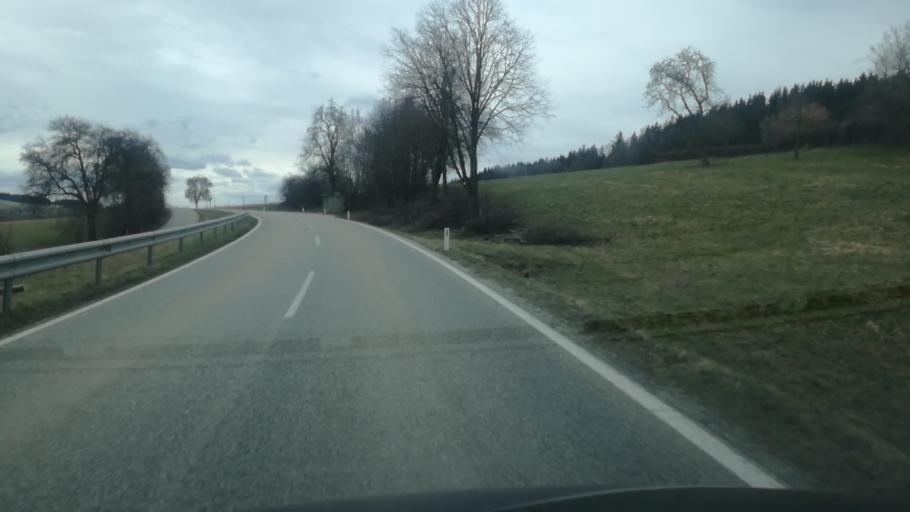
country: AT
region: Upper Austria
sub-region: Politischer Bezirk Ried im Innkreis
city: Ried im Innkreis
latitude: 48.1756
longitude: 13.4833
